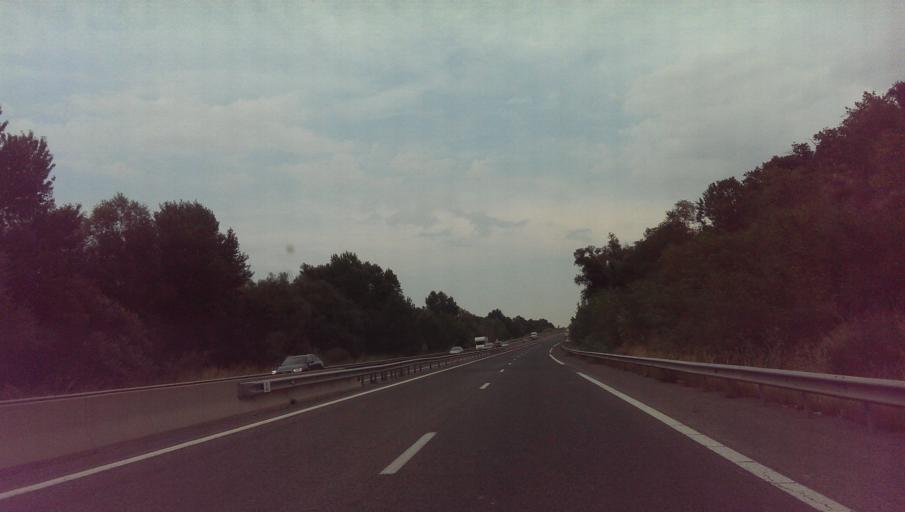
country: FR
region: Languedoc-Roussillon
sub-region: Departement des Pyrenees-Orientales
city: Pezilla-la-Riviere
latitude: 42.6833
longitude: 2.7698
